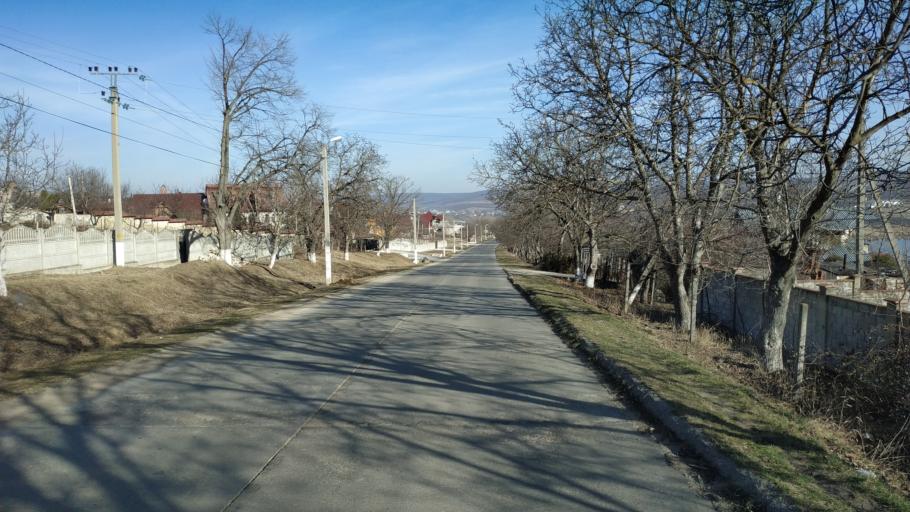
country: MD
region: Chisinau
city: Vatra
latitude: 46.9914
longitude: 28.6737
